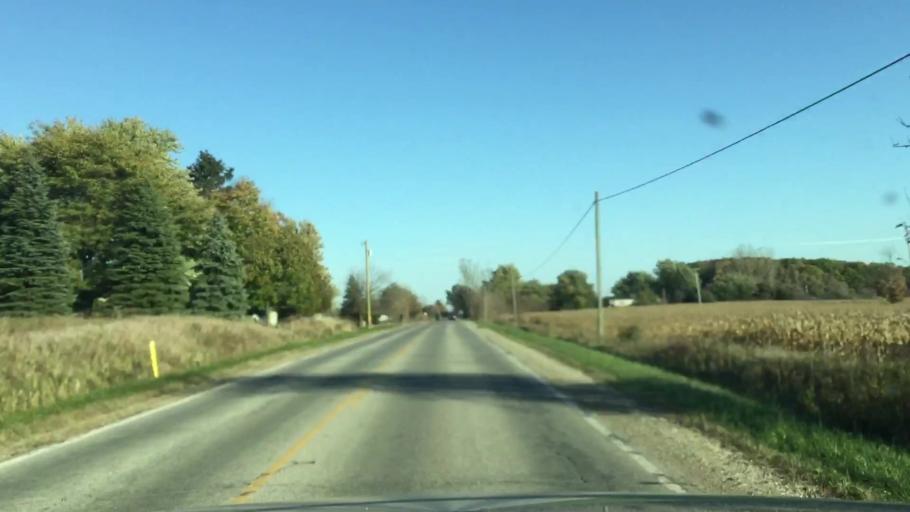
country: US
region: Michigan
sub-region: Lapeer County
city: North Branch
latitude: 43.3122
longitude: -83.1939
